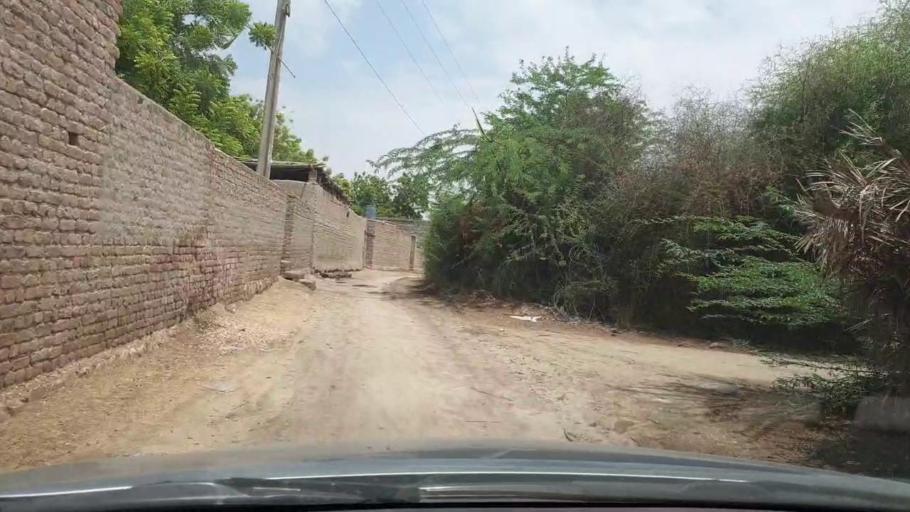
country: PK
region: Sindh
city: Kot Diji
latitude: 27.4292
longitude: 68.7517
